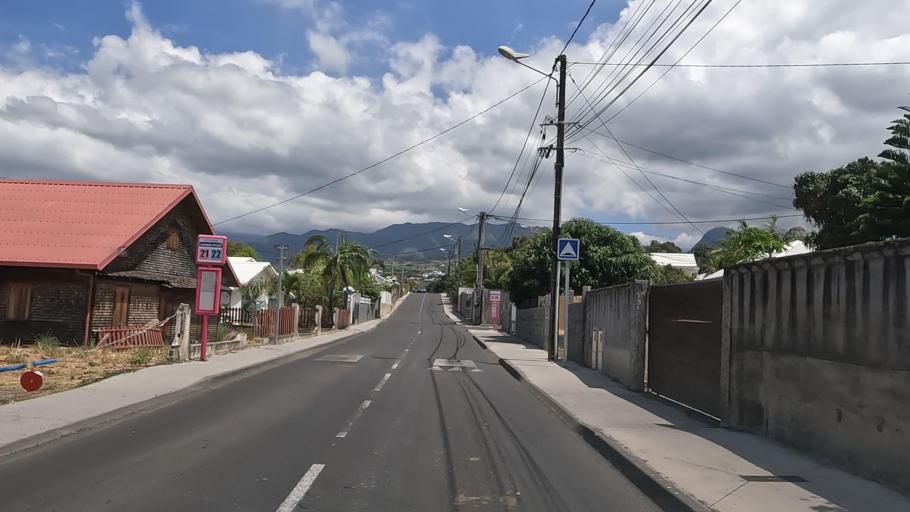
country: RE
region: Reunion
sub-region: Reunion
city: Saint-Louis
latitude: -21.2777
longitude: 55.4499
